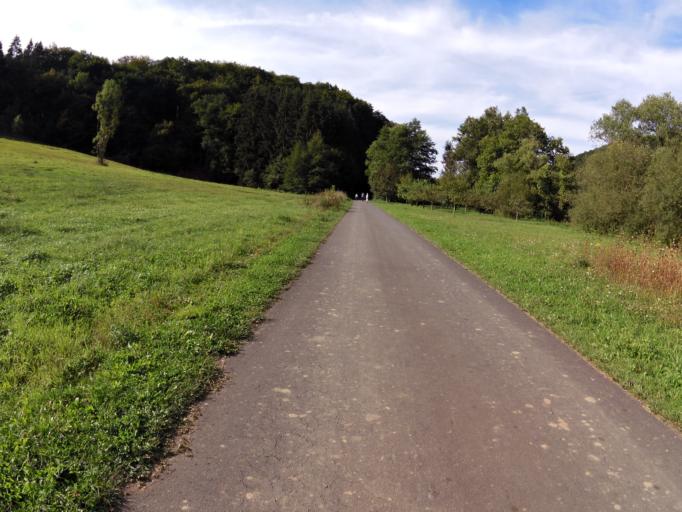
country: DE
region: Rheinland-Pfalz
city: Prumzurlay
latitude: 49.8778
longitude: 6.4323
